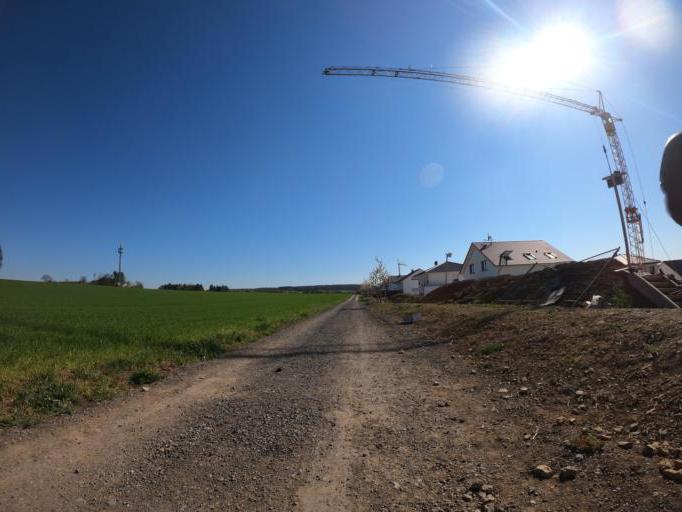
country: DE
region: Baden-Wuerttemberg
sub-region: Karlsruhe Region
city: Monsheim
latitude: 48.8947
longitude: 8.8838
